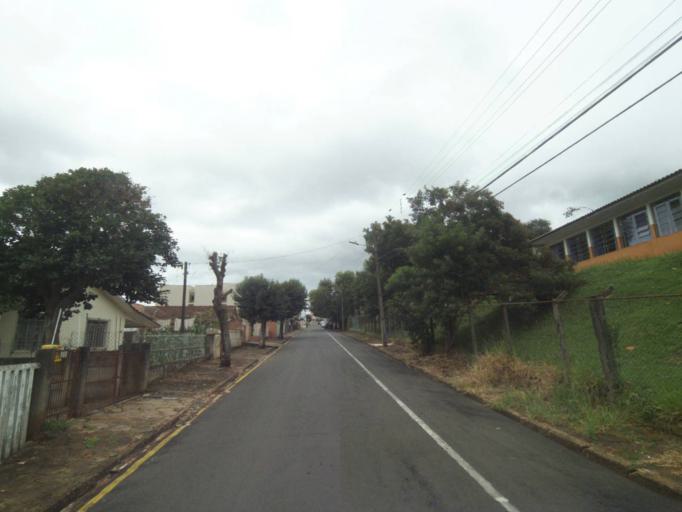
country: BR
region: Parana
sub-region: Telemaco Borba
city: Telemaco Borba
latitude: -24.3311
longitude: -50.6140
